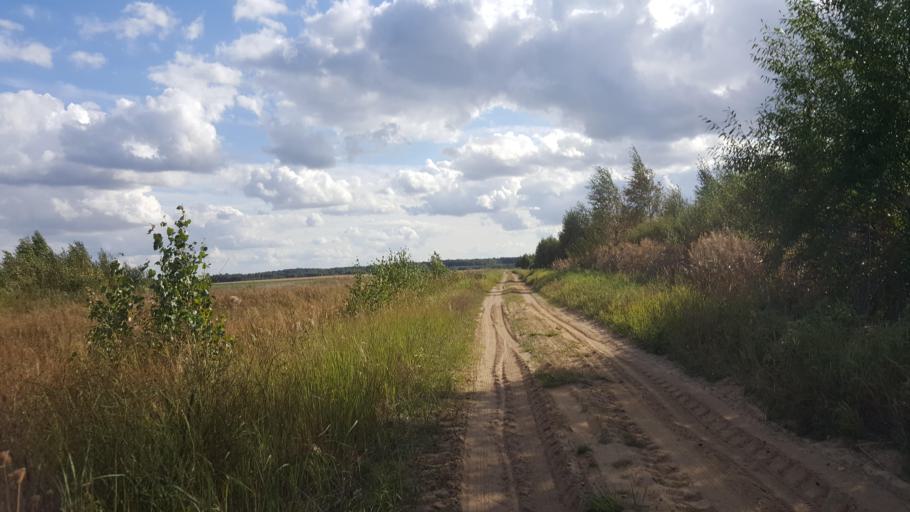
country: BY
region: Brest
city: Kamyanyets
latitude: 52.4553
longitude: 23.9347
